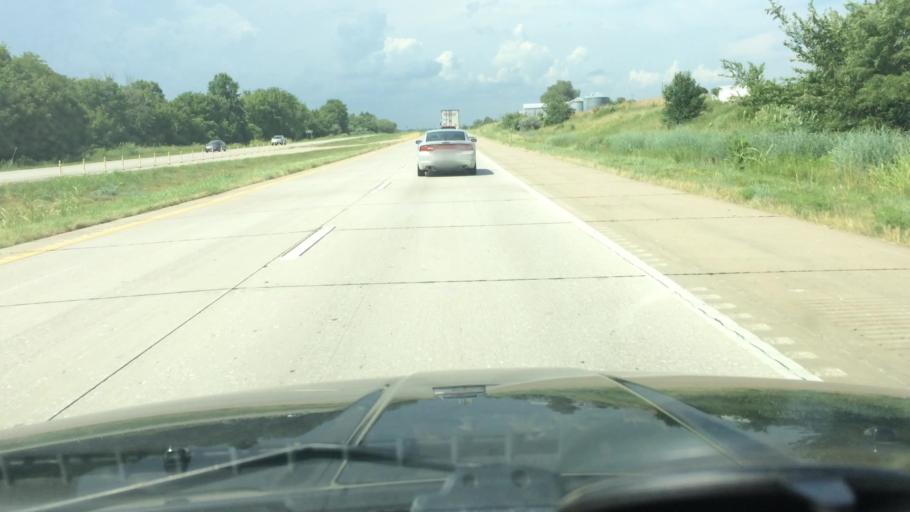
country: US
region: Missouri
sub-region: Henry County
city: Clinton
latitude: 38.3042
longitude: -93.7584
